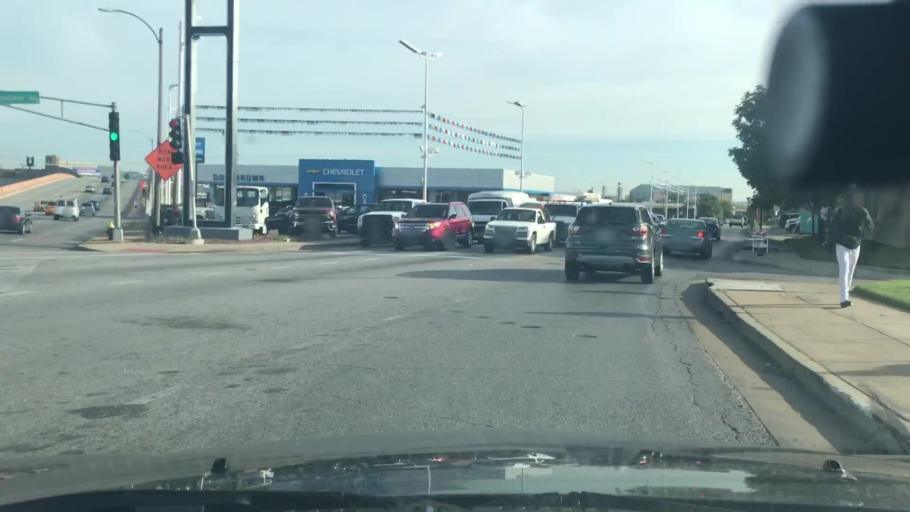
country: US
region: Missouri
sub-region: Saint Louis County
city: Richmond Heights
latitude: 38.6127
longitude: -90.2675
